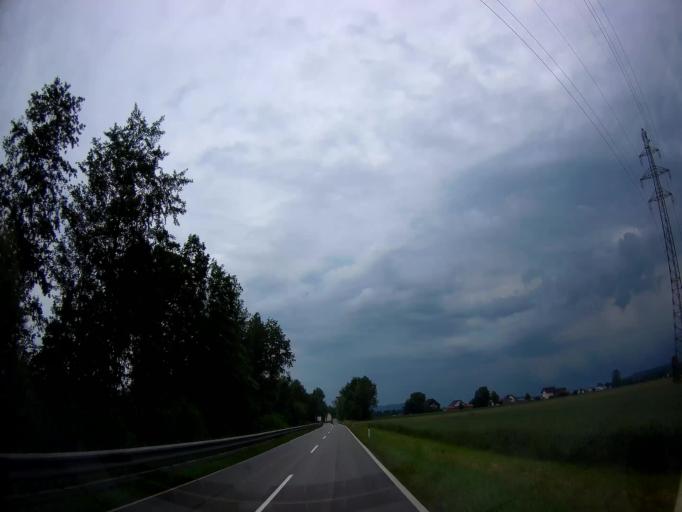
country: AT
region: Upper Austria
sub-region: Politischer Bezirk Braunau am Inn
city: Altheim
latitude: 48.1358
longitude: 13.1404
